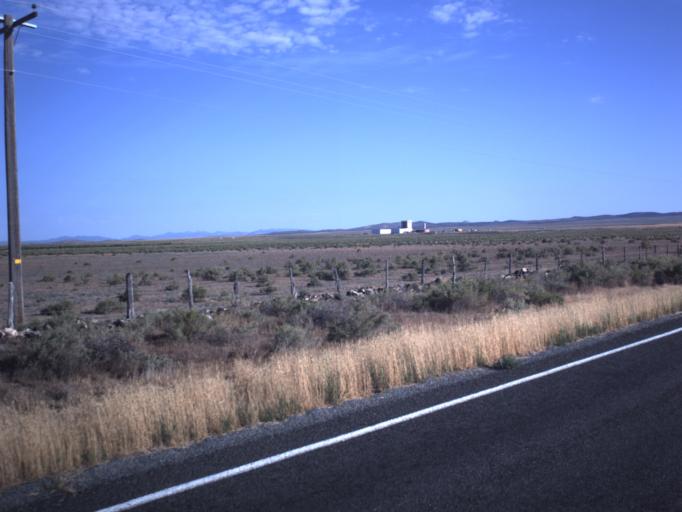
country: US
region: Utah
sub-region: Iron County
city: Enoch
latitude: 37.8629
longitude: -113.0316
